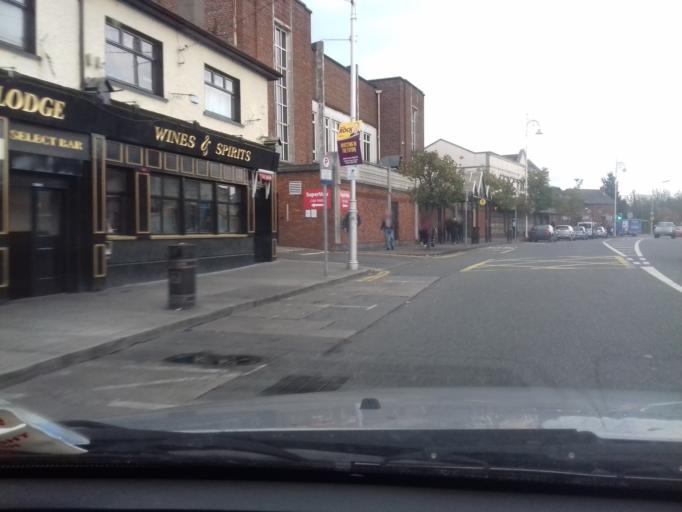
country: IE
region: Leinster
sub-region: Dublin City
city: Finglas
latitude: 53.3902
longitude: -6.2999
